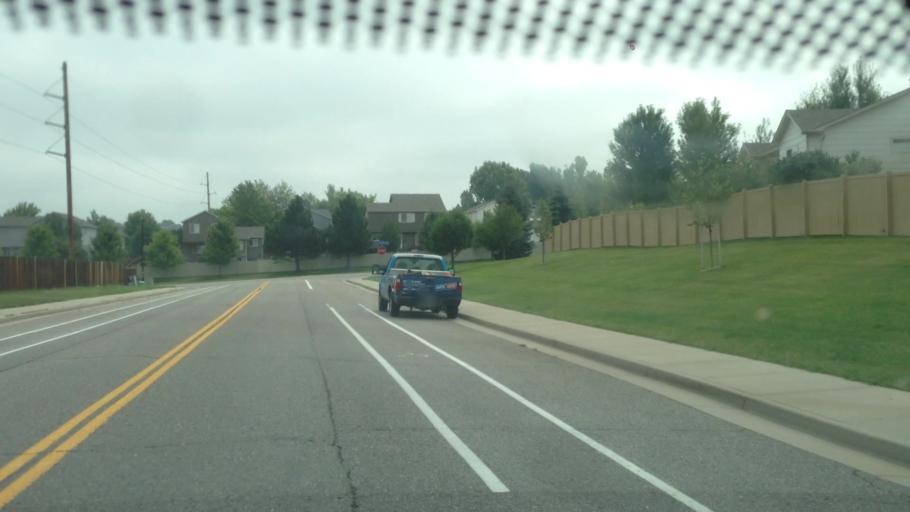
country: US
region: Colorado
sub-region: Douglas County
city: Parker
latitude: 39.6093
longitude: -104.7317
